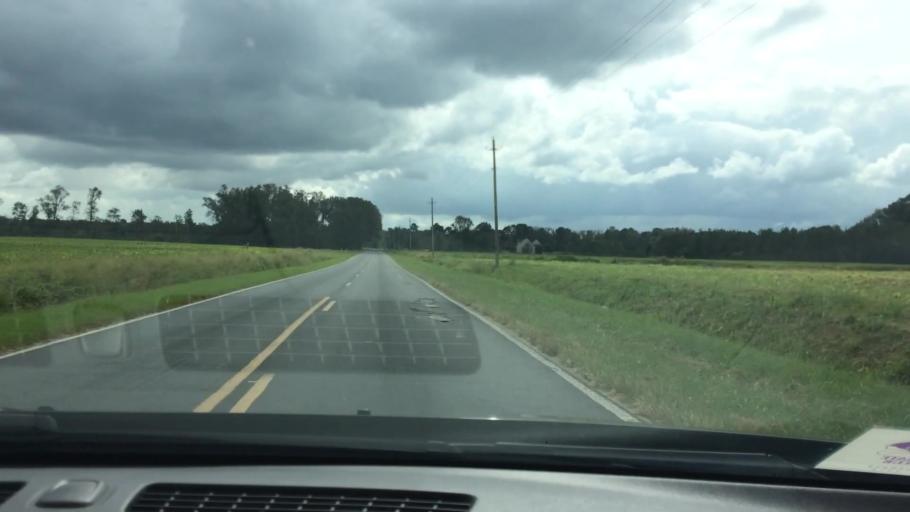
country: US
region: North Carolina
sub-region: Pitt County
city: Farmville
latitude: 35.5438
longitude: -77.5450
